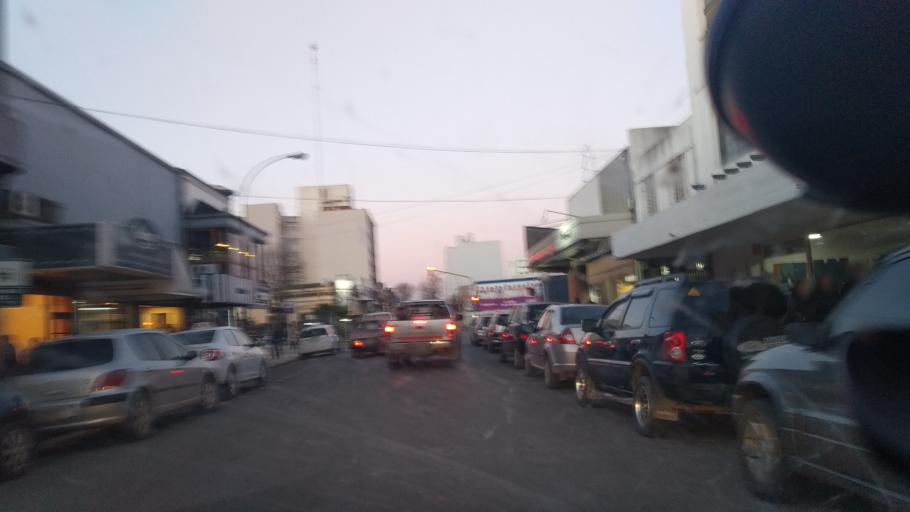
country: AR
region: Buenos Aires
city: Necochea
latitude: -38.5533
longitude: -58.7418
